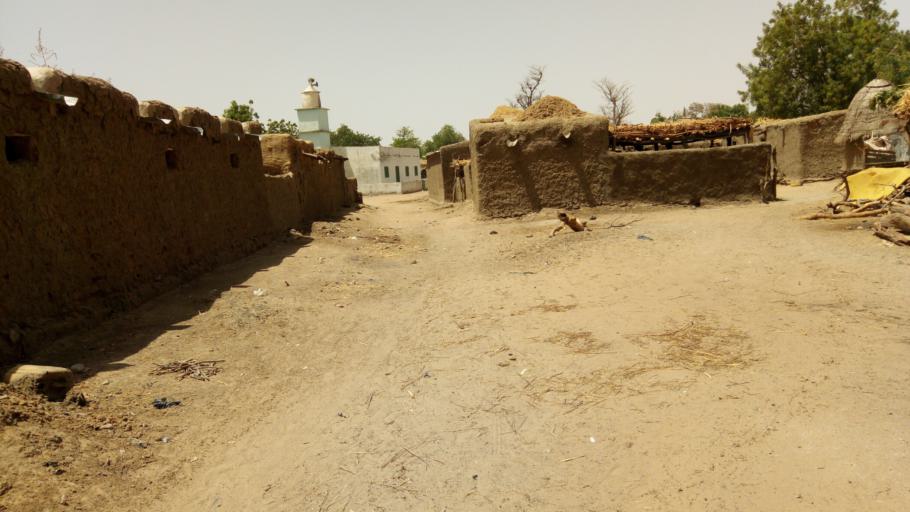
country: ML
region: Kayes
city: Diema
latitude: 14.4929
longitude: -9.0149
